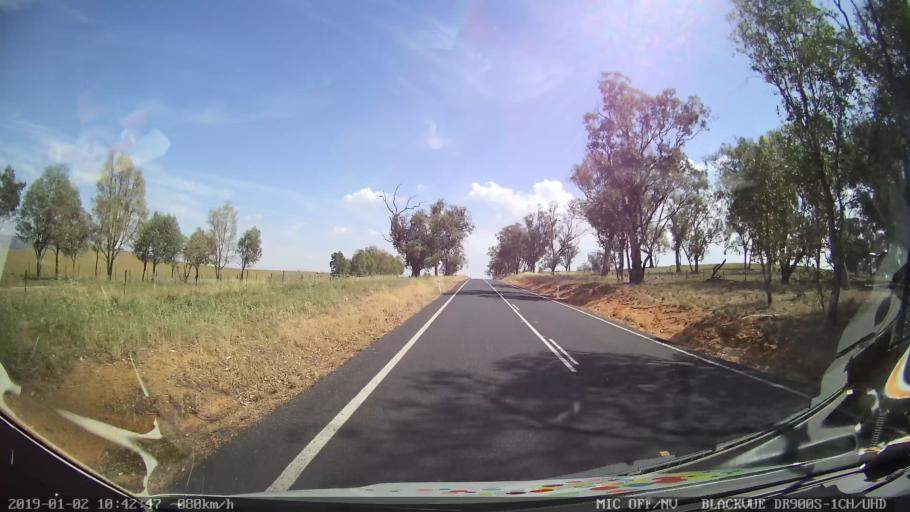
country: AU
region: New South Wales
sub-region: Cootamundra
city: Cootamundra
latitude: -34.7801
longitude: 148.3065
